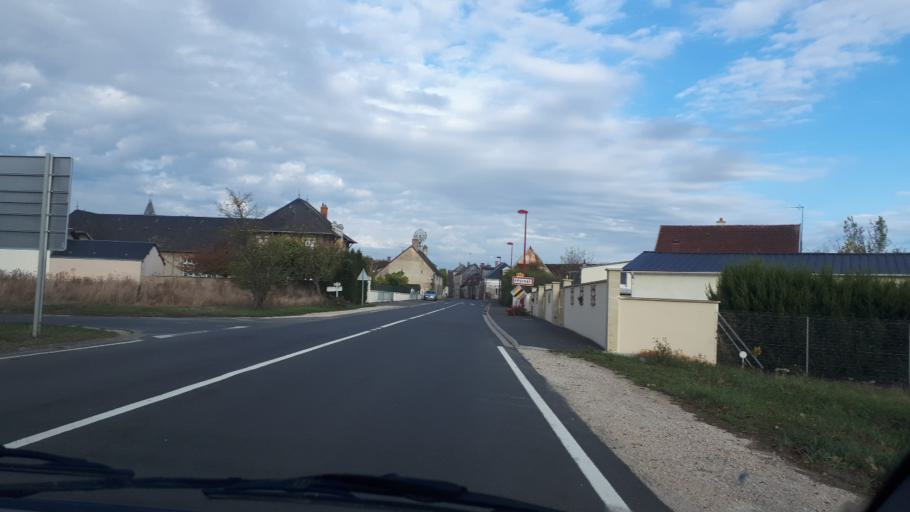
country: FR
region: Centre
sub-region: Departement du Loir-et-Cher
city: Aze
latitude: 47.8993
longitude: 0.9324
